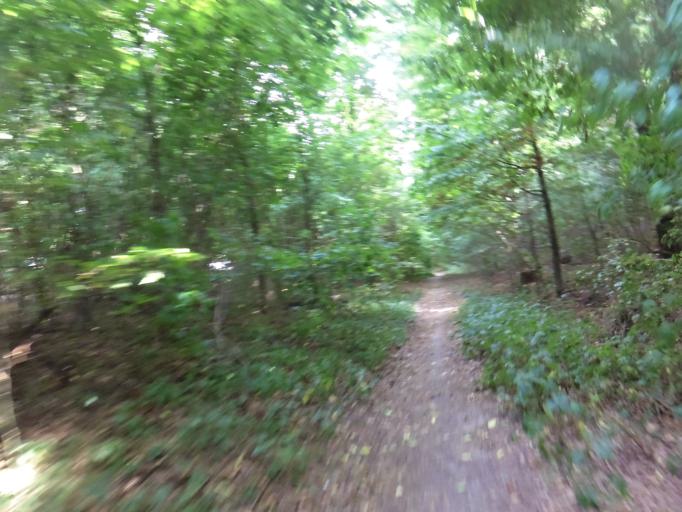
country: DE
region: Bavaria
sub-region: Regierungsbezirk Unterfranken
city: Hochberg
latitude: 49.7897
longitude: 9.8818
